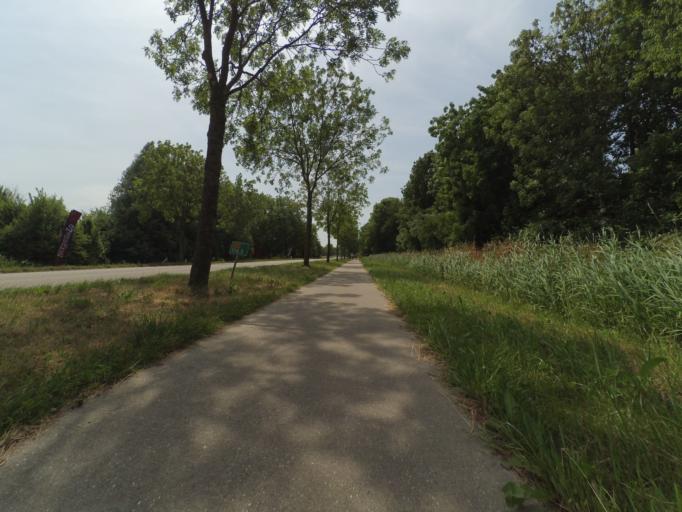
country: NL
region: North Brabant
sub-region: Gemeente Steenbergen
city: Welberg
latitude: 51.5929
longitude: 4.3343
